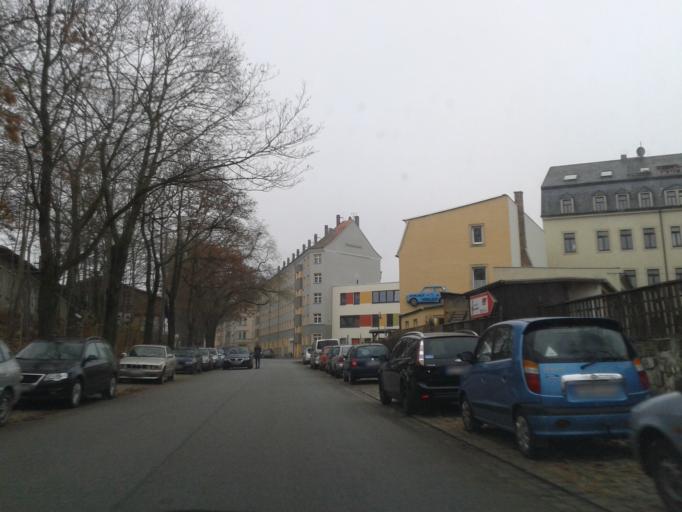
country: DE
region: Saxony
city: Dresden
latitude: 51.0759
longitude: 13.7295
